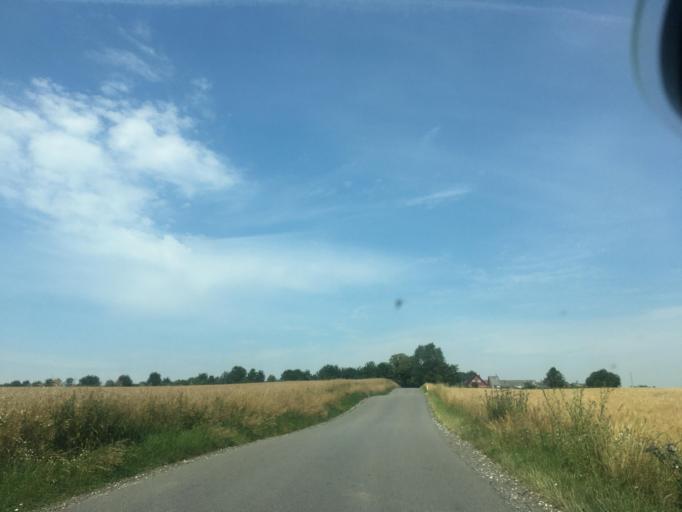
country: DK
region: Zealand
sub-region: Faxe Kommune
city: Ronnede
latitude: 55.2038
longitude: 12.0271
